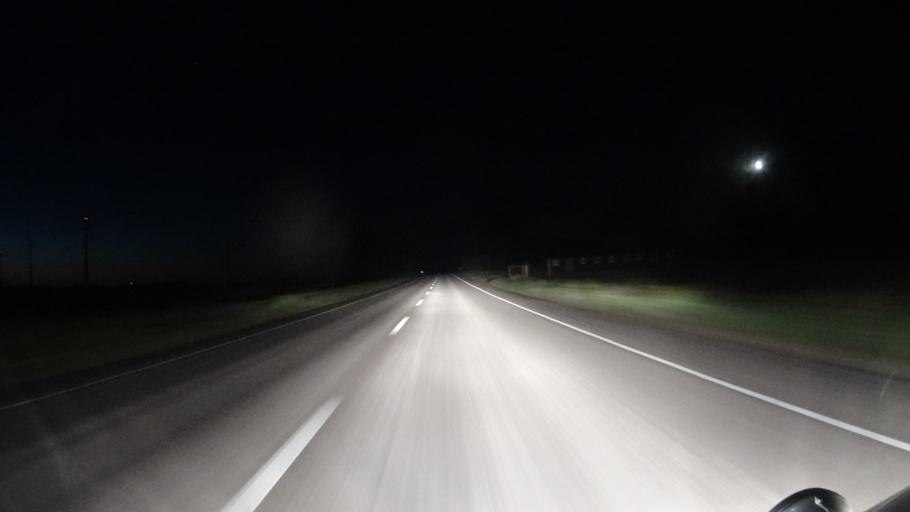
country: SE
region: OEstergoetland
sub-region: Vadstena Kommun
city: Herrestad
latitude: 58.2955
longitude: 14.7948
